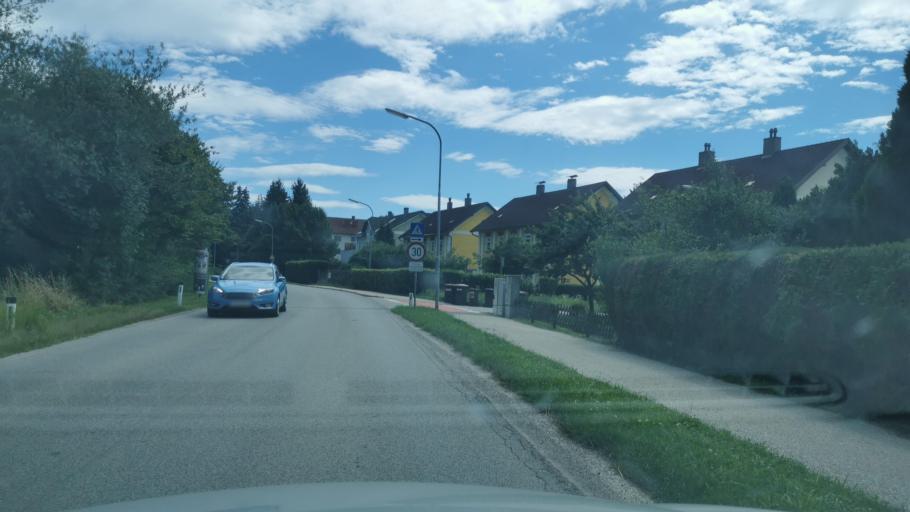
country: AT
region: Lower Austria
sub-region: Sankt Polten Stadt
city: Sankt Poelten
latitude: 48.1628
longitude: 15.6378
